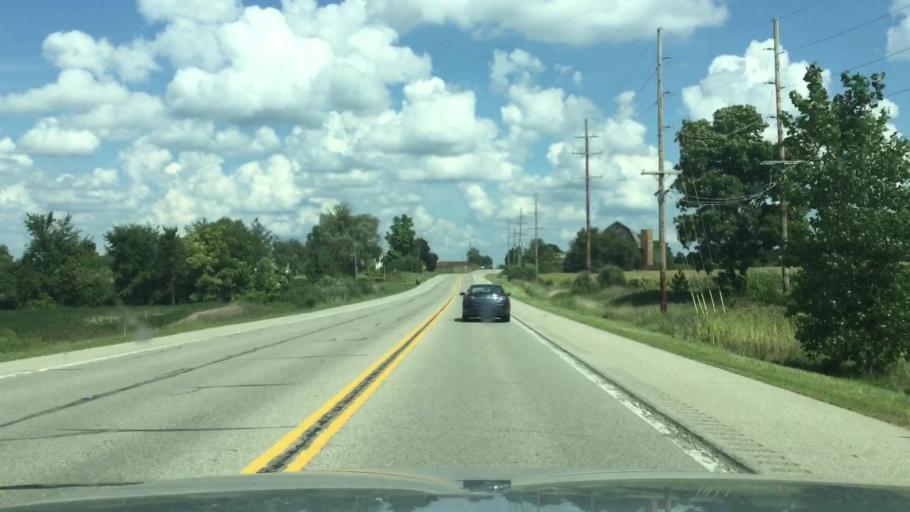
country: US
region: Michigan
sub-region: Washtenaw County
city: Saline
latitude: 42.1407
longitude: -83.8436
